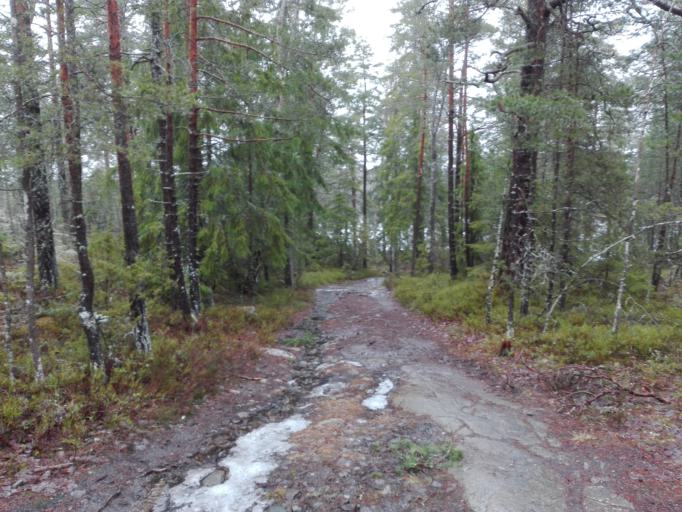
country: SE
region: Stockholm
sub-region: Nacka Kommun
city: Fisksatra
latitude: 59.2757
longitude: 18.2551
